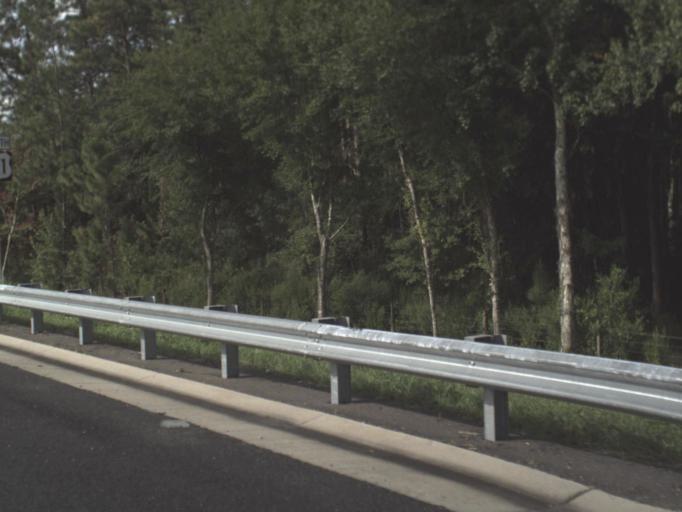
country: US
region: Florida
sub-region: Pasco County
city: Land O' Lakes
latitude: 28.2879
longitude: -82.4881
